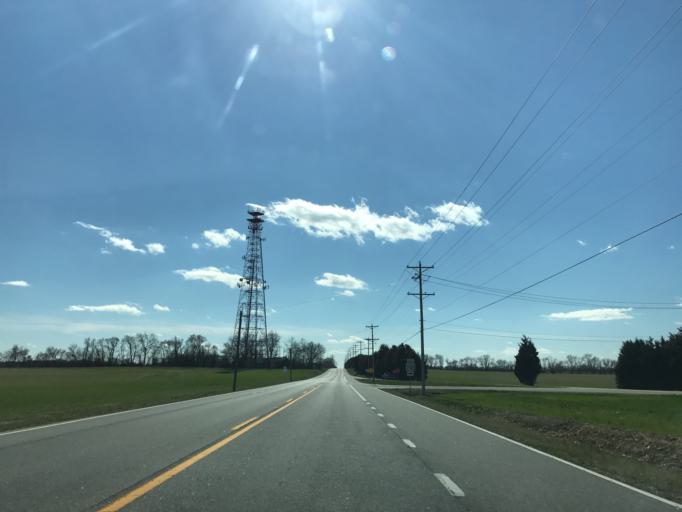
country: US
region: Maryland
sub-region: Kent County
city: Rock Hall
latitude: 39.2138
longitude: -76.1740
